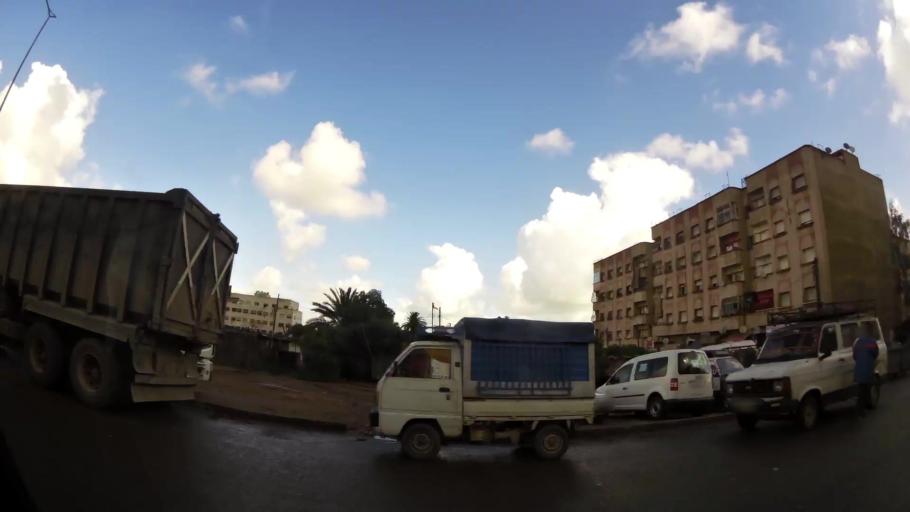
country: MA
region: Grand Casablanca
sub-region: Mediouna
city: Tit Mellil
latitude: 33.5823
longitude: -7.5374
